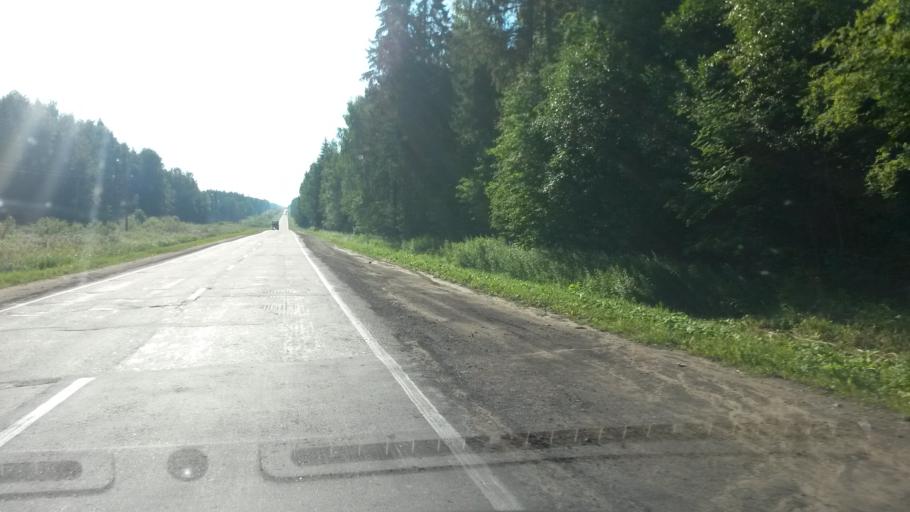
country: RU
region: Jaroslavl
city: Gavrilov-Yam
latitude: 57.2679
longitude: 39.9819
